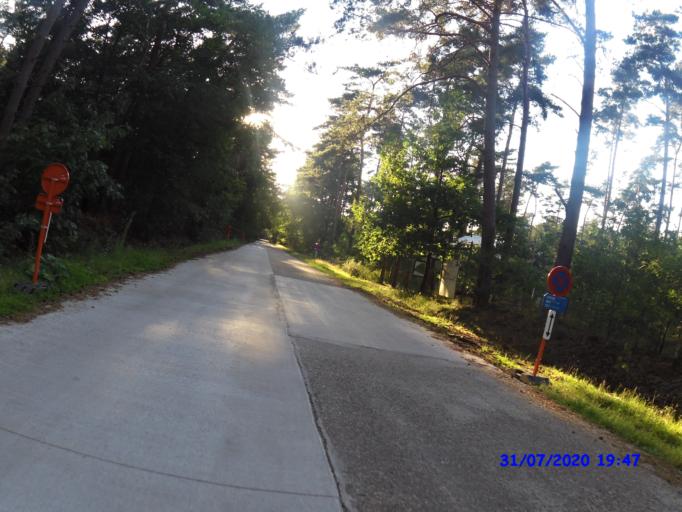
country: BE
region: Flanders
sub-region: Provincie Antwerpen
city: Kasterlee
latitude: 51.2384
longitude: 4.9479
